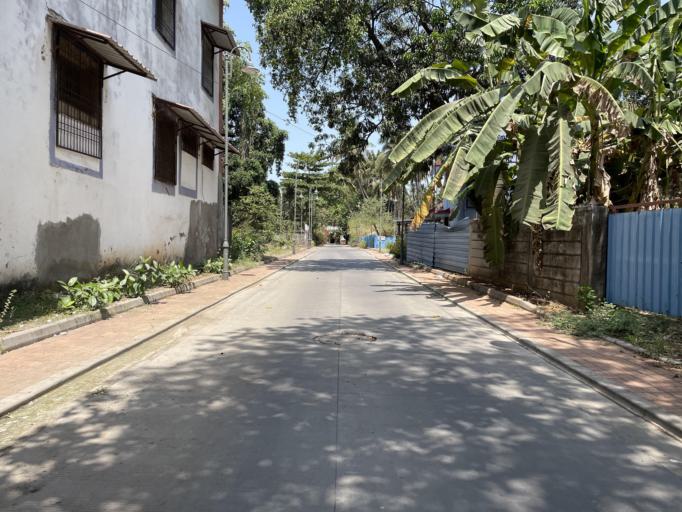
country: IN
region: Daman and Diu
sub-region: Daman District
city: Daman
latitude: 20.4066
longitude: 72.8335
